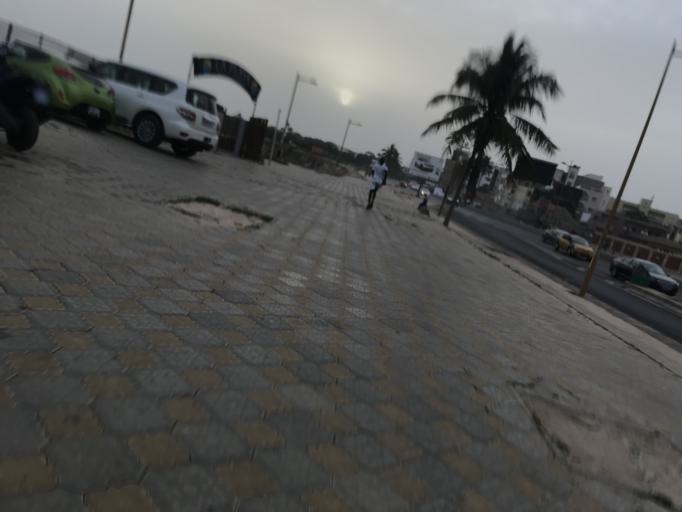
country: SN
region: Dakar
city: Dakar
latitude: 14.6736
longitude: -17.4507
